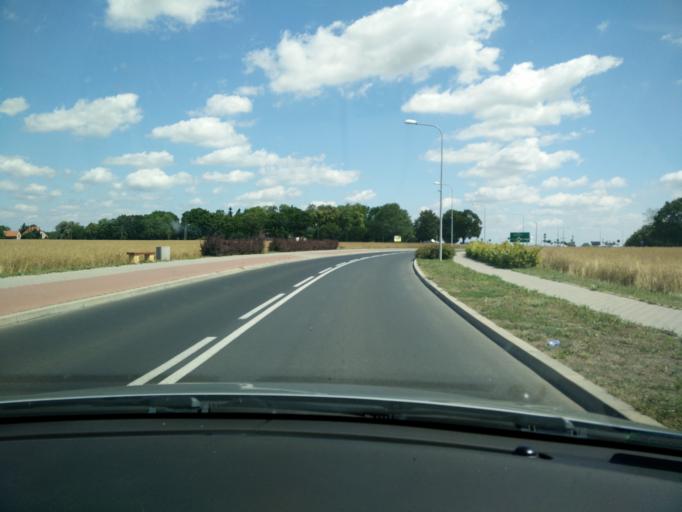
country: PL
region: Greater Poland Voivodeship
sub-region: Powiat sredzki
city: Sroda Wielkopolska
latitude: 52.2379
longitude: 17.2721
